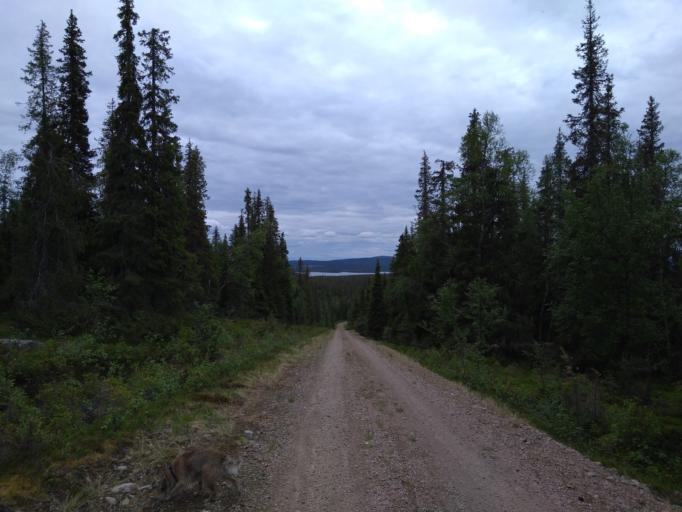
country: FI
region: Lapland
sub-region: Tunturi-Lappi
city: Muonio
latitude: 67.9666
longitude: 24.0802
